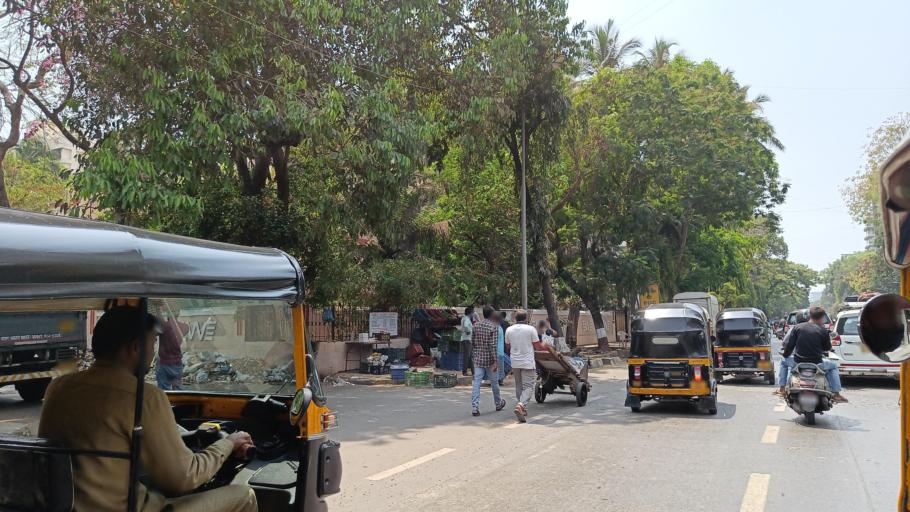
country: IN
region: Maharashtra
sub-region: Mumbai Suburban
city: Mumbai
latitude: 19.0801
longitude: 72.8345
